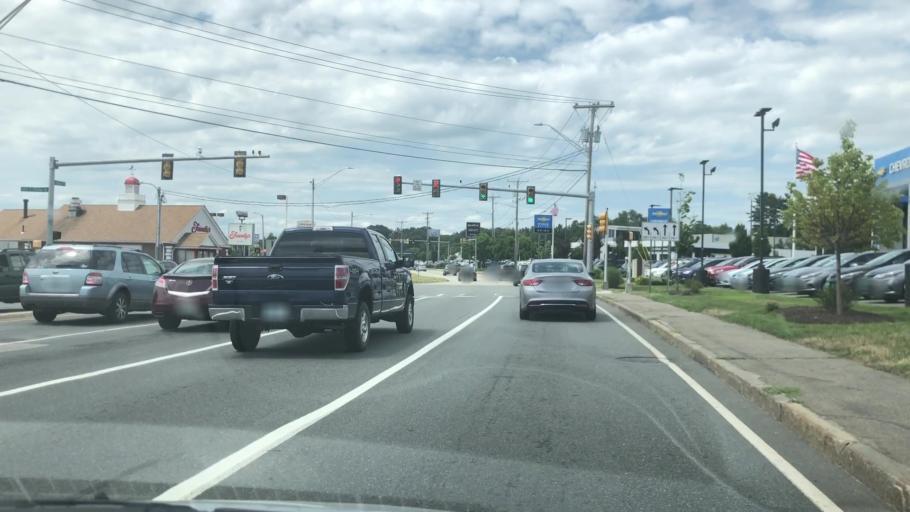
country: US
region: New Hampshire
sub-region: Hillsborough County
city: Manchester
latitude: 42.9595
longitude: -71.4368
